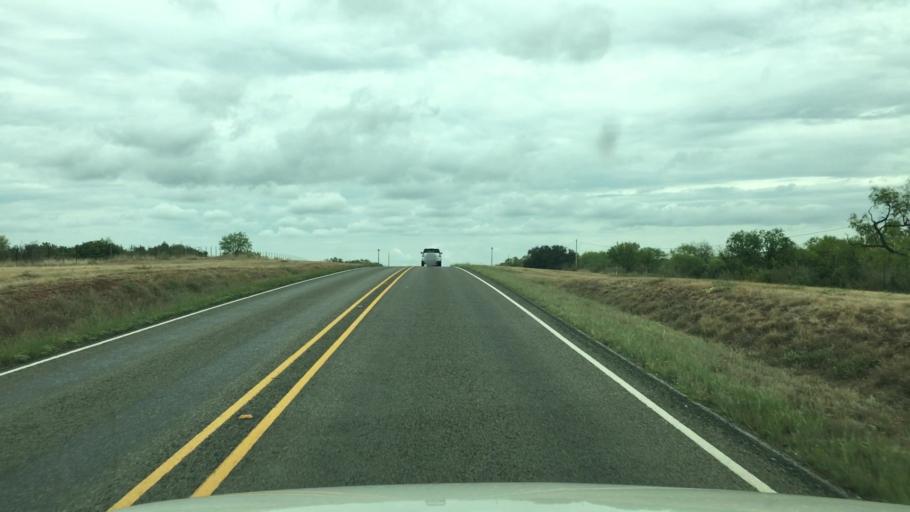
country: US
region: Texas
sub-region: Llano County
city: Kingsland
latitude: 30.5755
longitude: -98.4919
